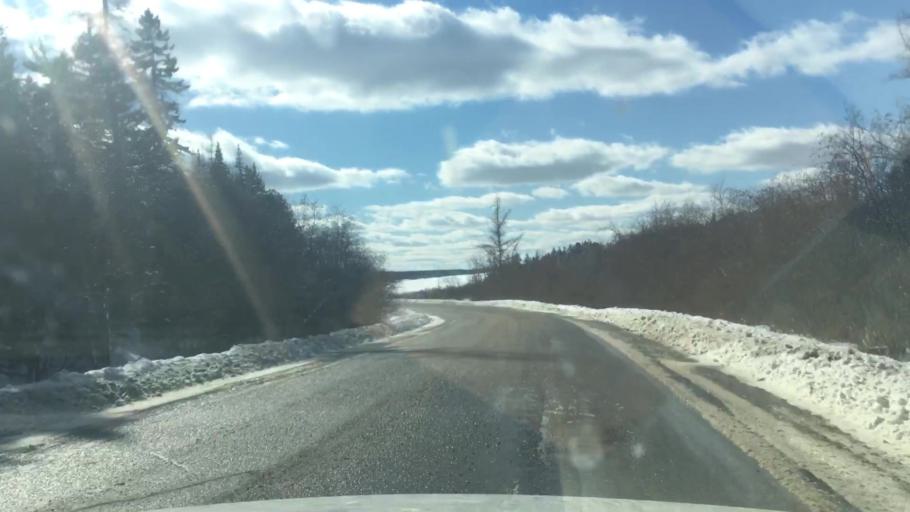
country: US
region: Maine
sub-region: Washington County
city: Machiasport
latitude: 44.6742
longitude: -67.4213
